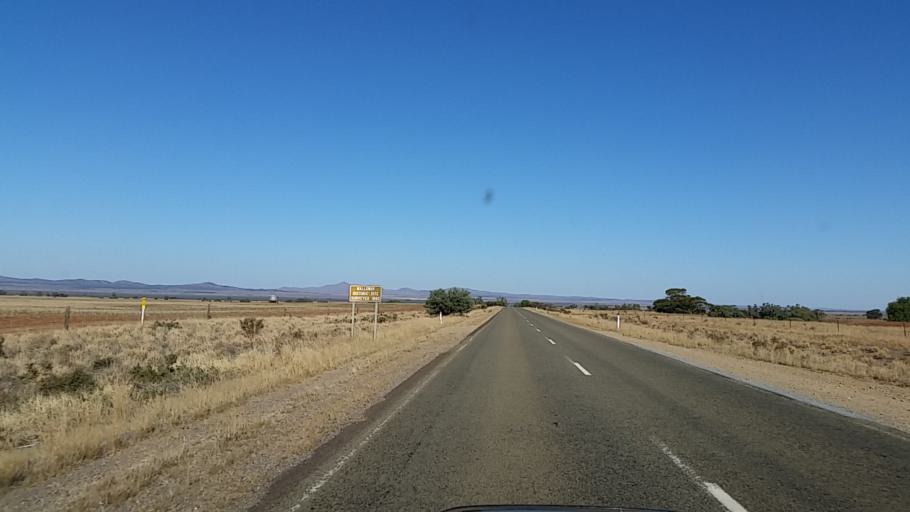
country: AU
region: South Australia
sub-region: Peterborough
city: Peterborough
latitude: -32.6314
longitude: 138.5916
